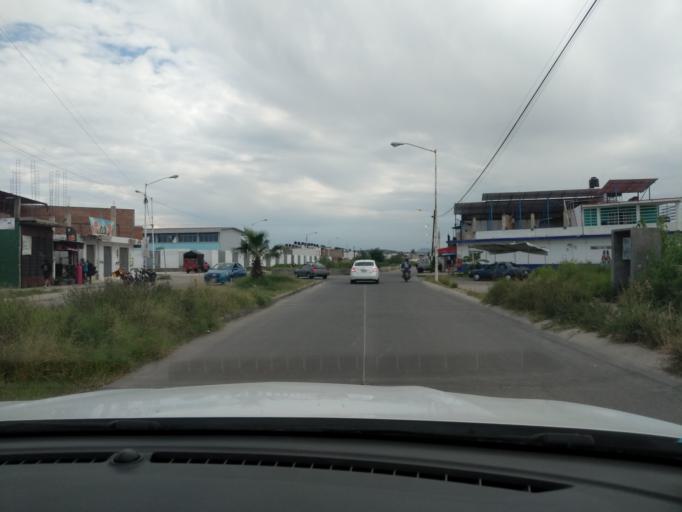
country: MX
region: Jalisco
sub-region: El Salto
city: Galaxia Bonito Jalisco
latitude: 20.5077
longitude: -103.1909
